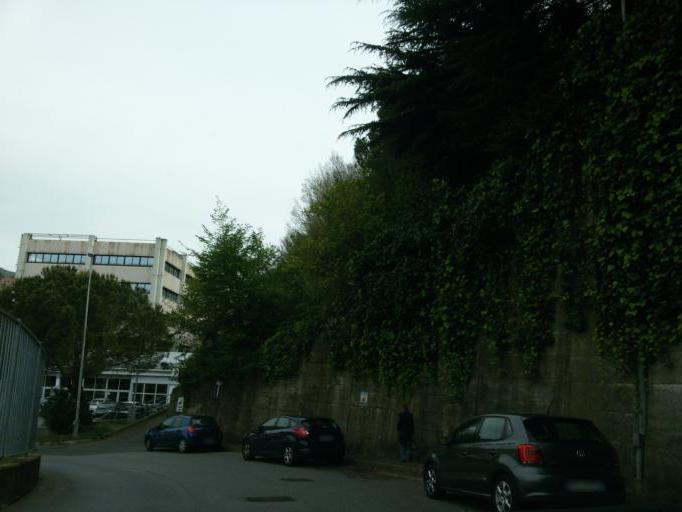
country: IT
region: Liguria
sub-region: Provincia di Genova
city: Piccarello
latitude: 44.4467
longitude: 8.9717
